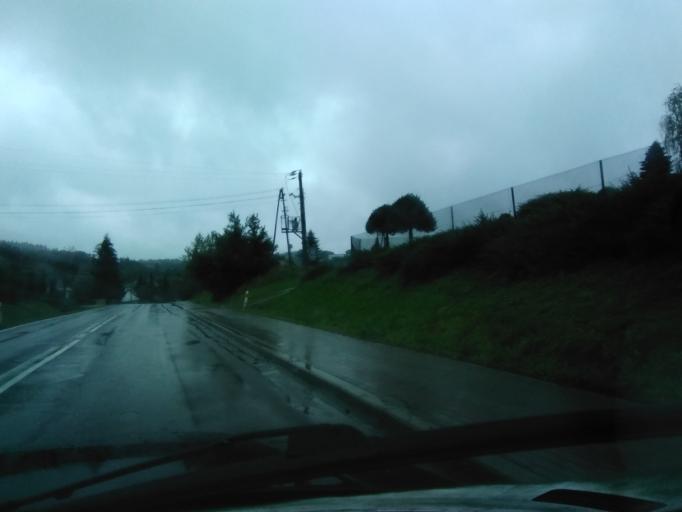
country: PL
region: Subcarpathian Voivodeship
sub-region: Powiat ropczycko-sedziszowski
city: Niedzwiada
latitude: 50.0258
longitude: 21.5467
